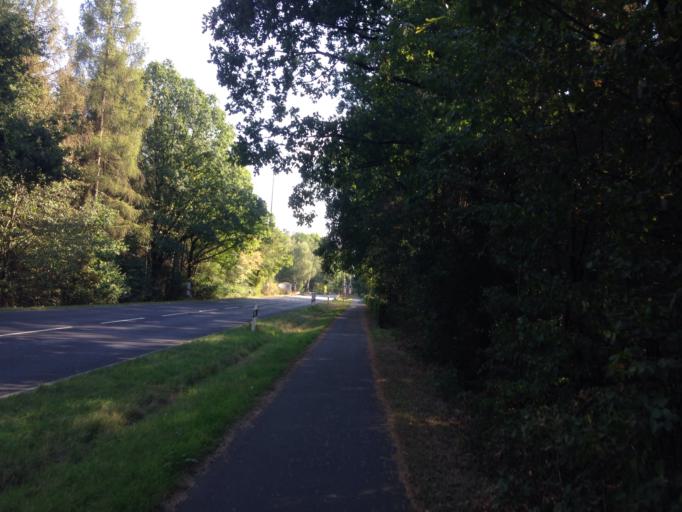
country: DE
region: Hesse
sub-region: Regierungsbezirk Giessen
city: Giessen
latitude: 50.5570
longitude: 8.6963
